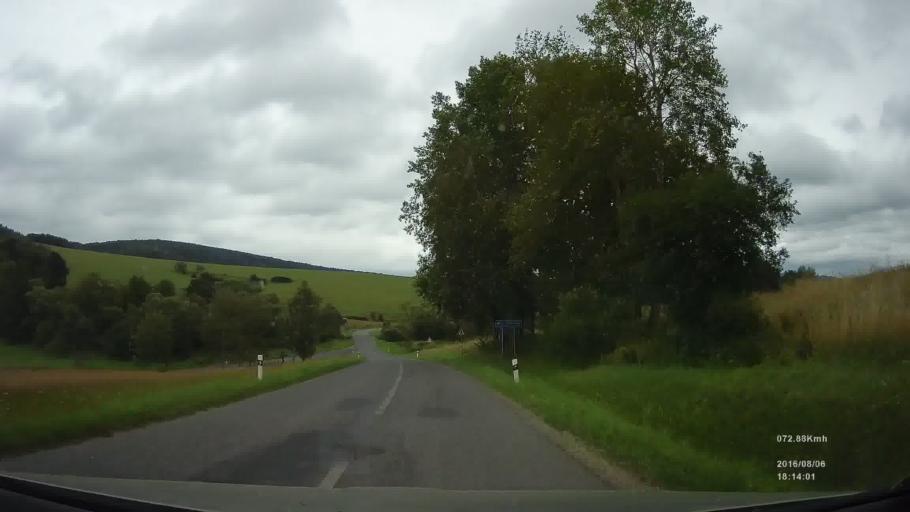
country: SK
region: Presovsky
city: Svidnik
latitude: 49.3568
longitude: 21.5933
